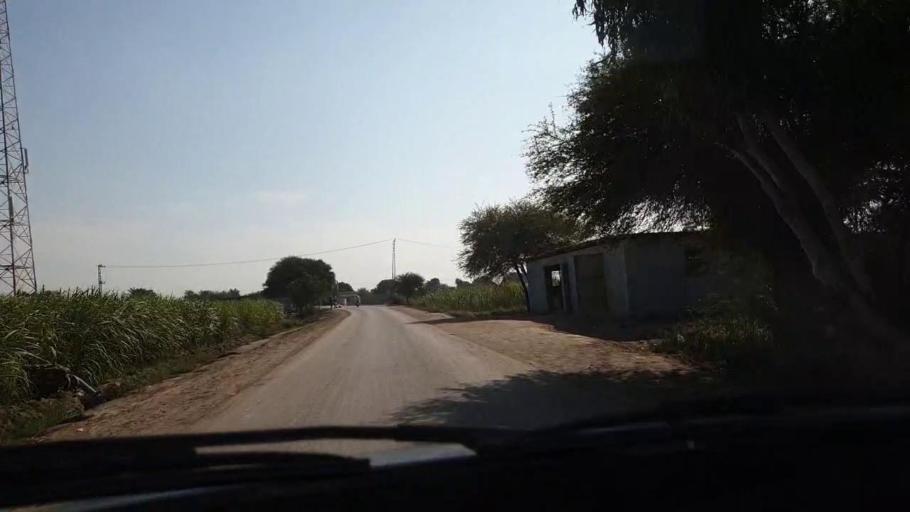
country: PK
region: Sindh
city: Bulri
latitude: 24.9587
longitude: 68.4195
